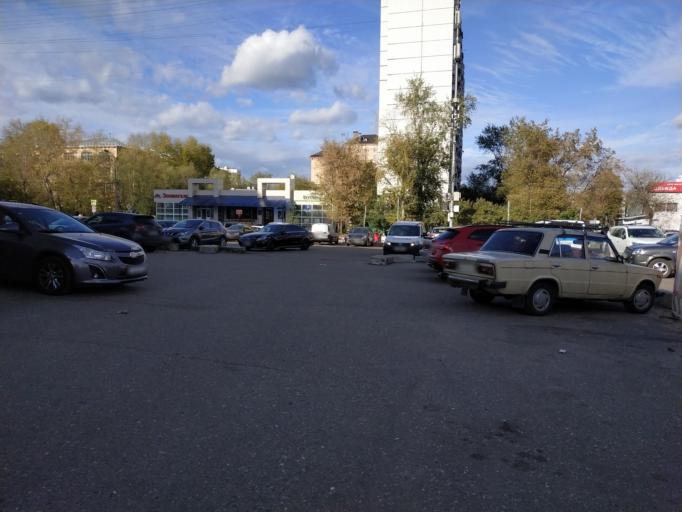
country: RU
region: Moskovskaya
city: Koptevo
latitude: 55.8084
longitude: 37.5285
